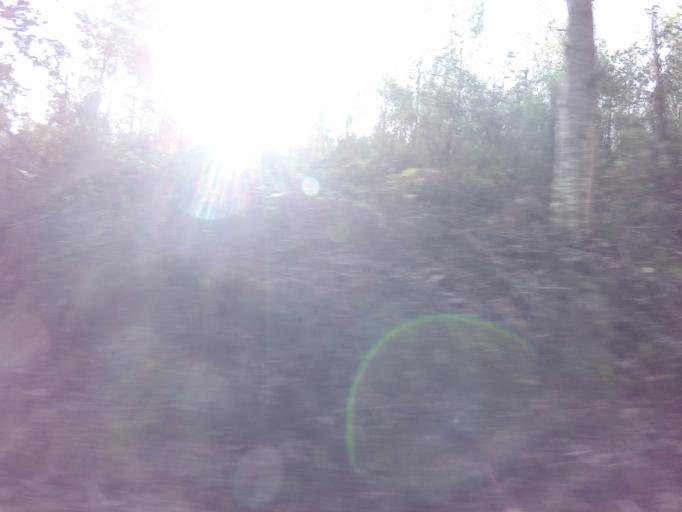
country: AU
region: Tasmania
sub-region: Derwent Valley
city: New Norfolk
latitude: -42.7794
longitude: 146.9016
